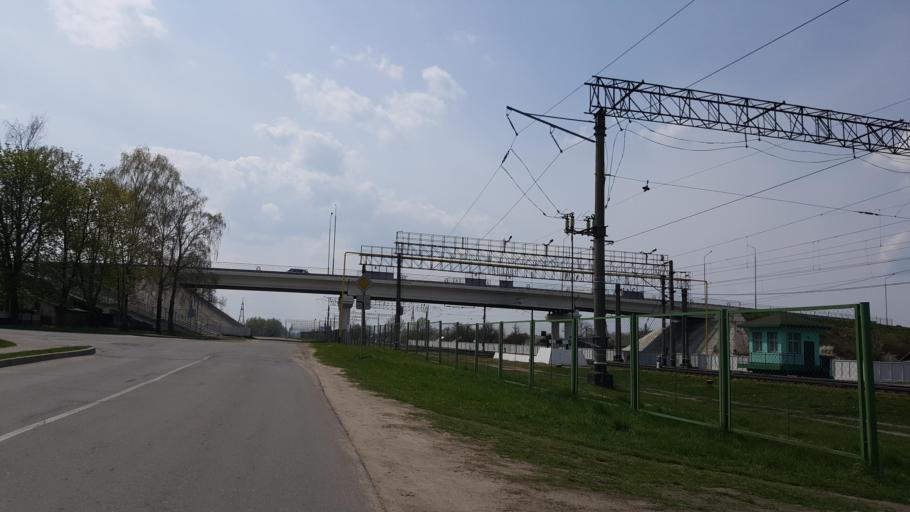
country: BY
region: Brest
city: Zhabinka
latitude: 52.1984
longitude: 24.0111
